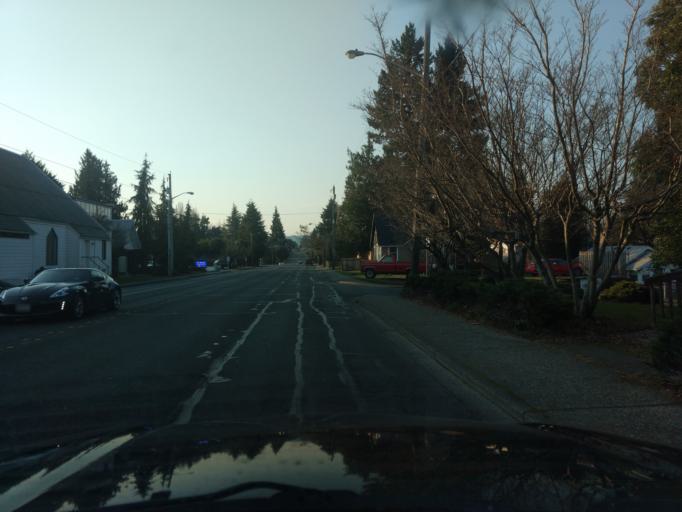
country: US
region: Washington
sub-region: Kitsap County
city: Bremerton
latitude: 47.5710
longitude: -122.6384
